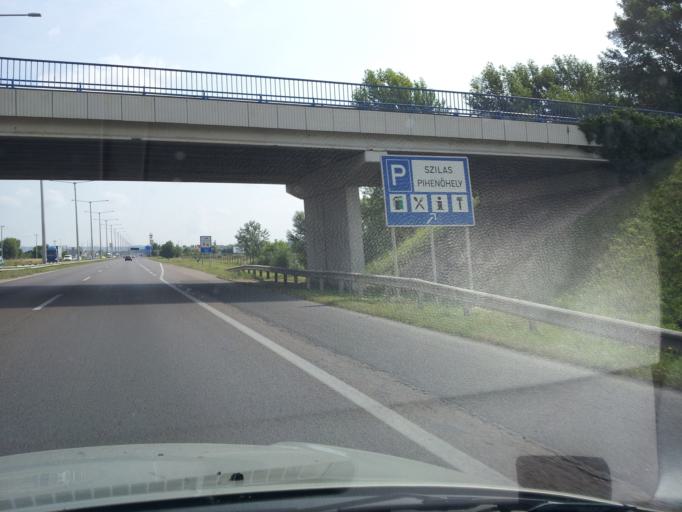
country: HU
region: Budapest
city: Budapest XV. keruelet
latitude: 47.5627
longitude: 19.1401
